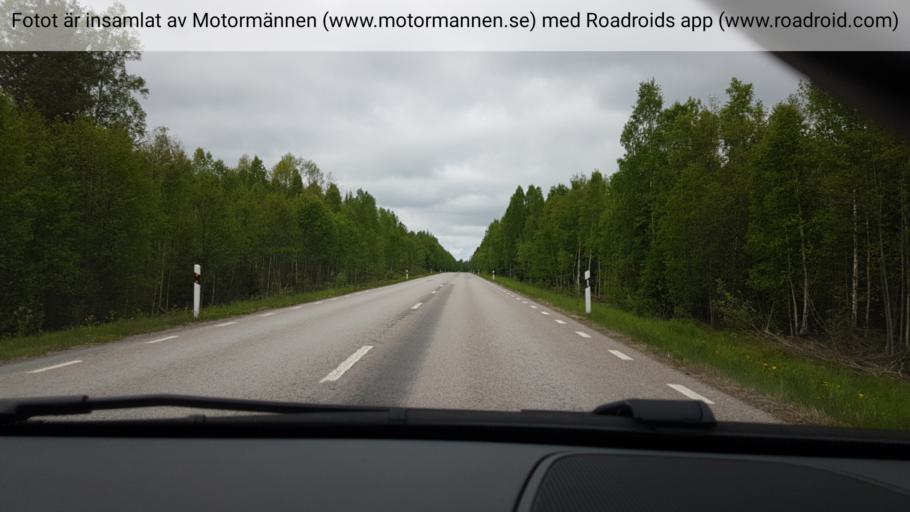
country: SE
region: Uppsala
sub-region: Tierps Kommun
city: Tierp
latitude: 60.3596
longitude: 17.3539
